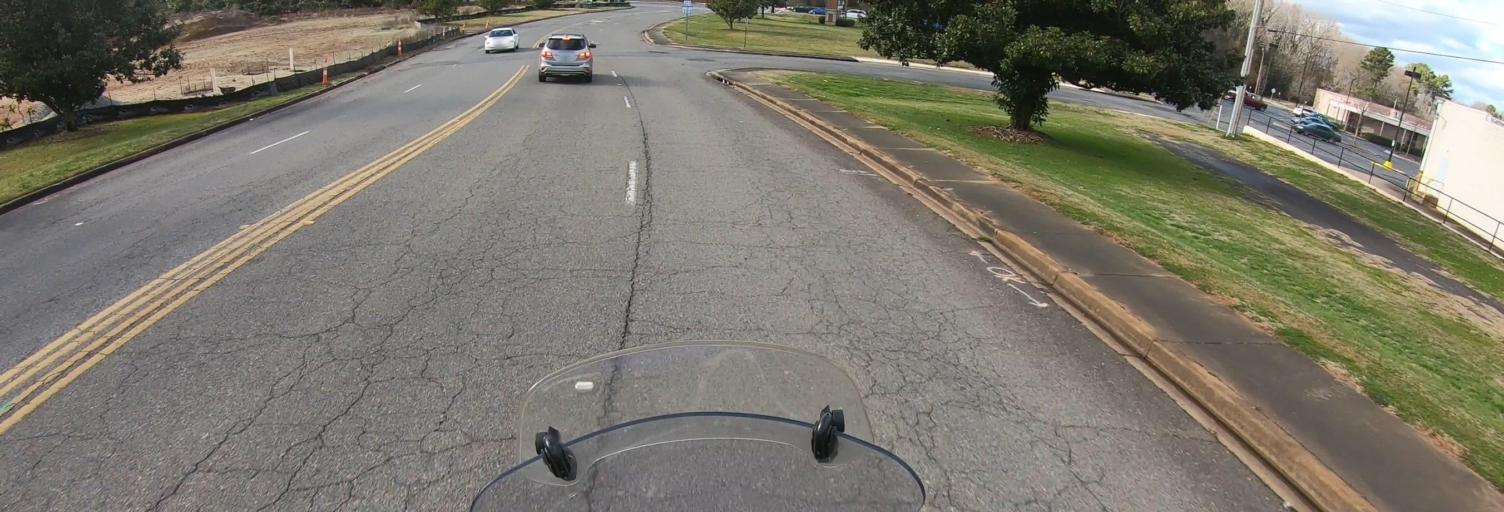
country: US
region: South Carolina
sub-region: York County
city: Rock Hill
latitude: 34.9492
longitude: -81.0187
